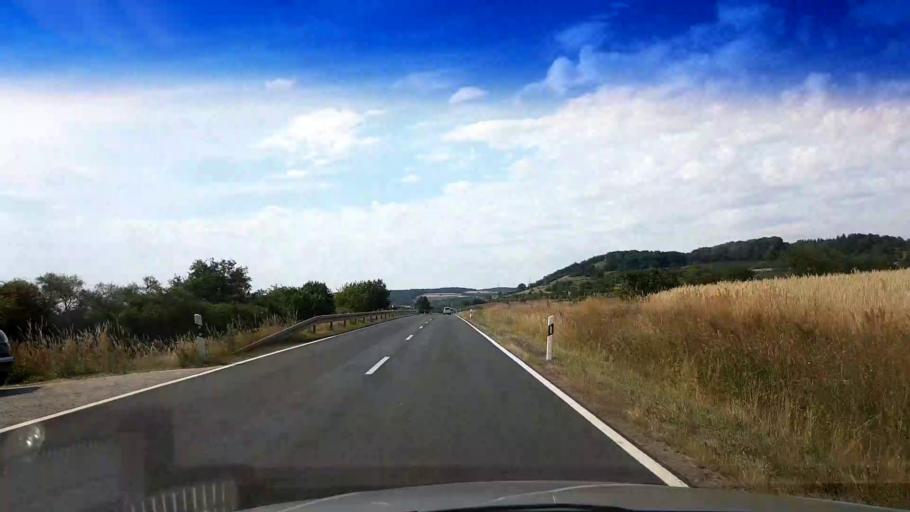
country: DE
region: Bavaria
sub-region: Regierungsbezirk Unterfranken
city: Stettfeld
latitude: 49.9518
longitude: 10.7417
